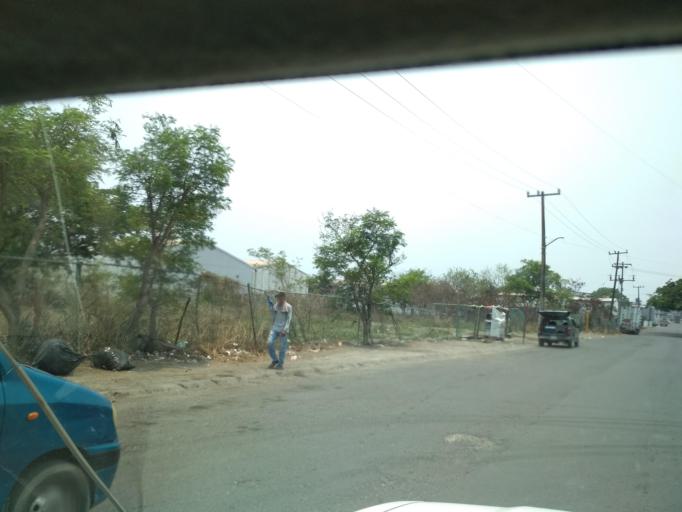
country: MX
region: Veracruz
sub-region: Veracruz
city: Lomas de Rio Medio Cuatro
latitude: 19.1674
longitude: -96.2398
